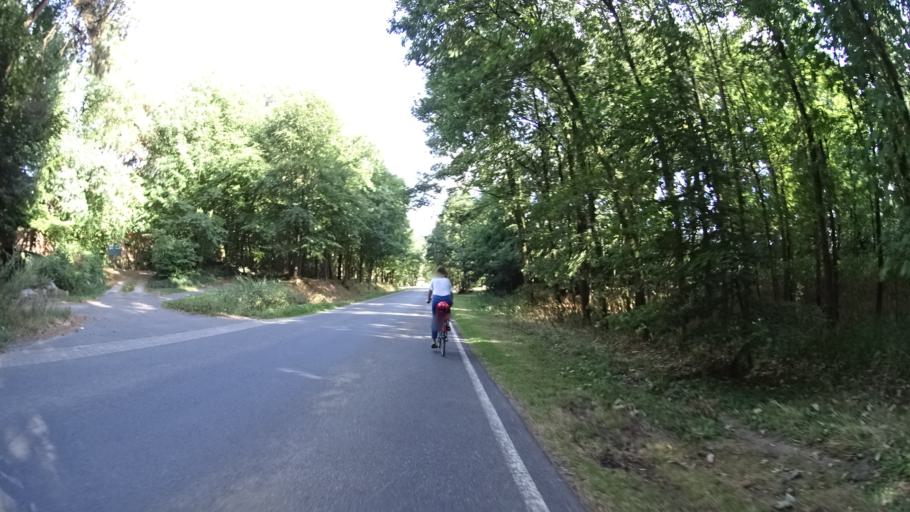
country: DE
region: Lower Saxony
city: Undeloh
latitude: 53.1479
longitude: 9.9100
